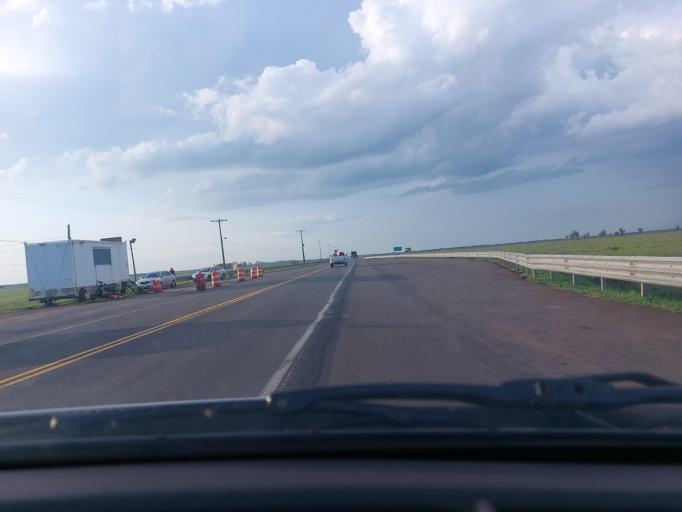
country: PY
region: Cordillera
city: Arroyos y Esteros
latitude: -25.0381
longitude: -57.0363
